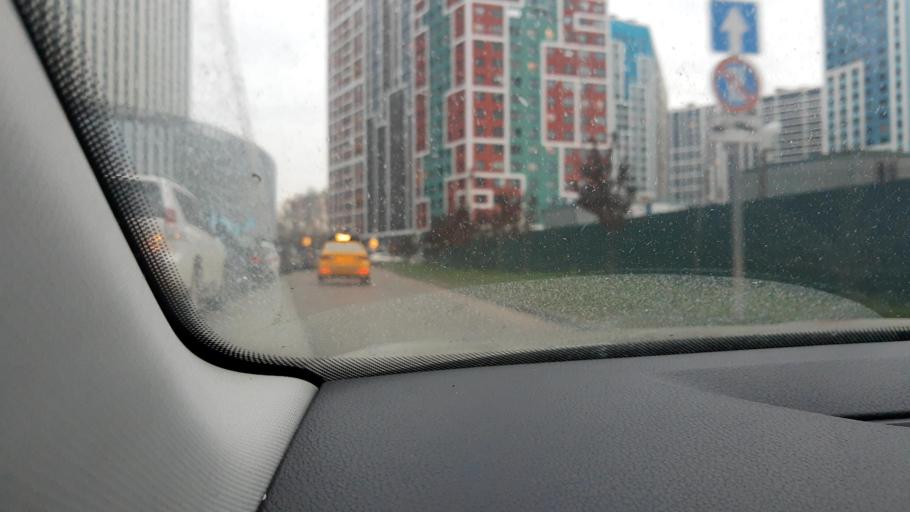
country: RU
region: Moscow
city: Annino
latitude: 55.5562
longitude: 37.5559
